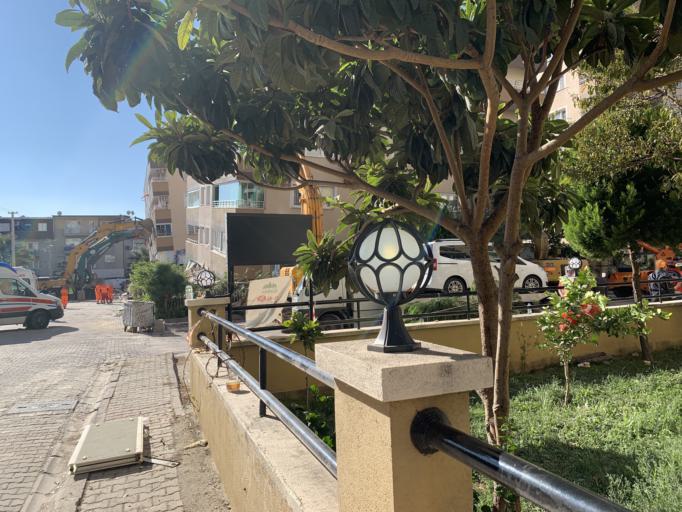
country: TR
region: Izmir
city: Bornova
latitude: 38.4613
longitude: 27.1804
